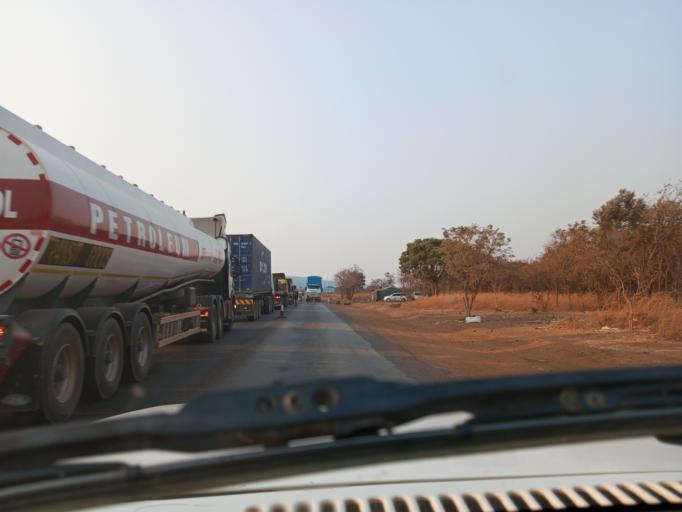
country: ZM
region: Northern
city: Mpika
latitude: -11.9177
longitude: 31.4162
